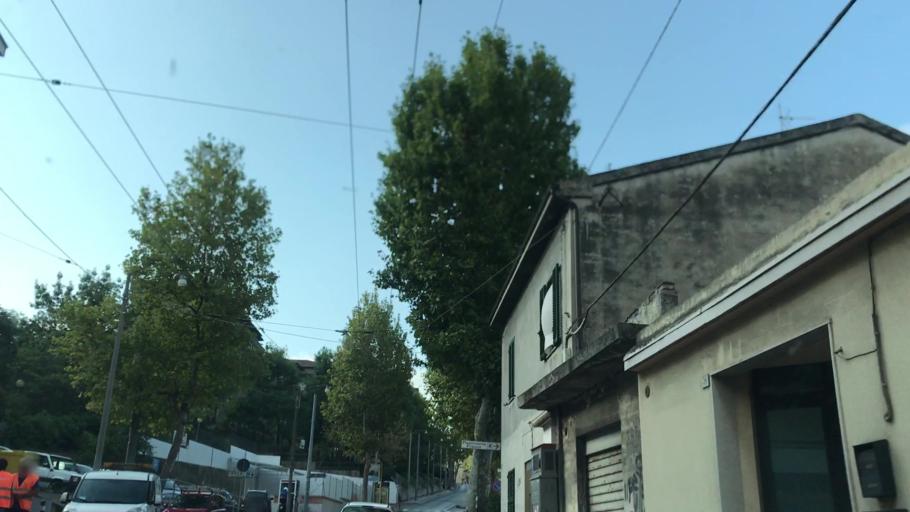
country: IT
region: The Marches
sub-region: Provincia di Ancona
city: Le Grazie di Ancona
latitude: 43.5966
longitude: 13.5174
